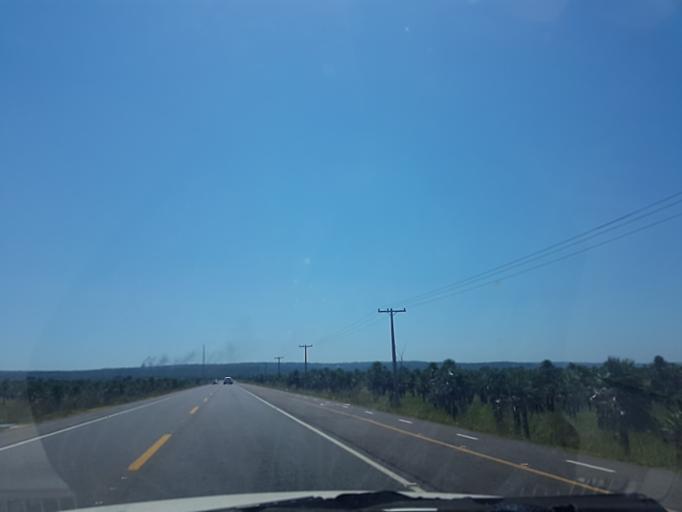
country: PY
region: Cordillera
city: Emboscada
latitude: -25.2079
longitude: -57.3812
